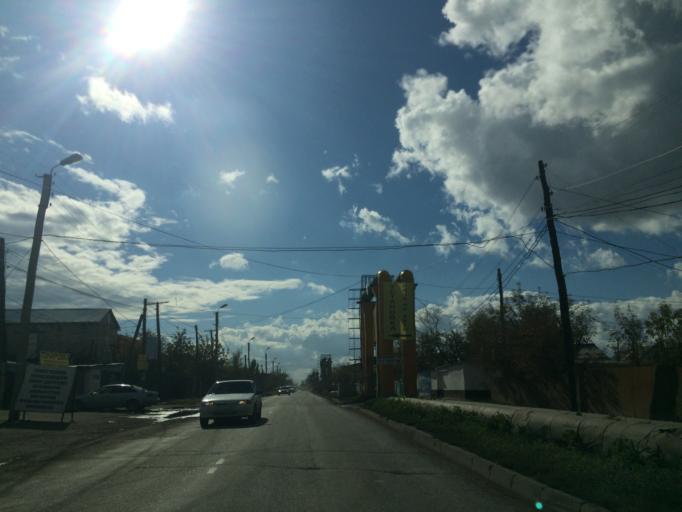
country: KZ
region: Astana Qalasy
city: Astana
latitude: 51.1905
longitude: 71.3939
